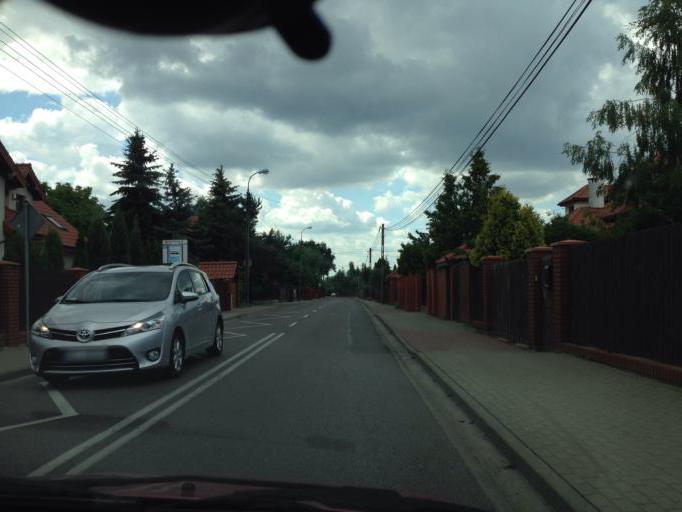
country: PL
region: Masovian Voivodeship
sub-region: Warszawa
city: Bemowo
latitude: 52.2469
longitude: 20.8836
